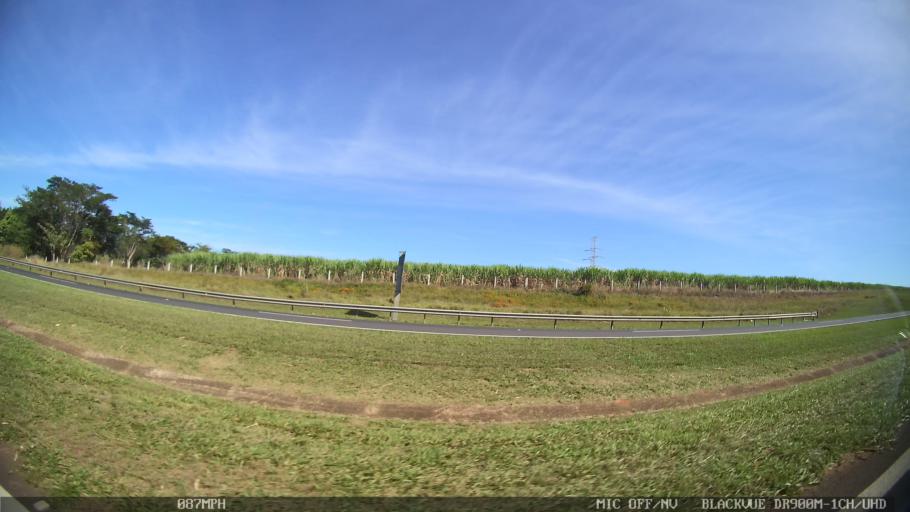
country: BR
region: Sao Paulo
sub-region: Porto Ferreira
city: Porto Ferreira
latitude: -21.9257
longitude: -47.4705
